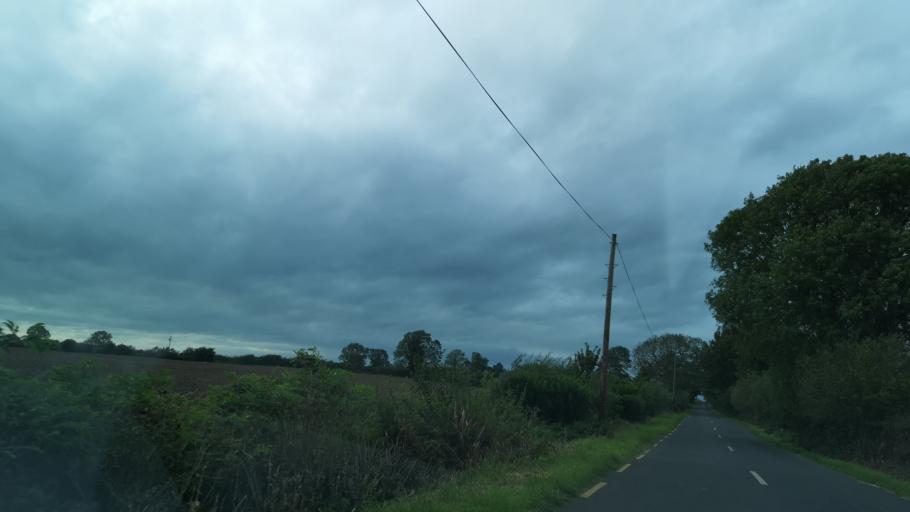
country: IE
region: Leinster
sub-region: Uibh Fhaili
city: Ferbane
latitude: 53.2001
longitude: -7.7815
